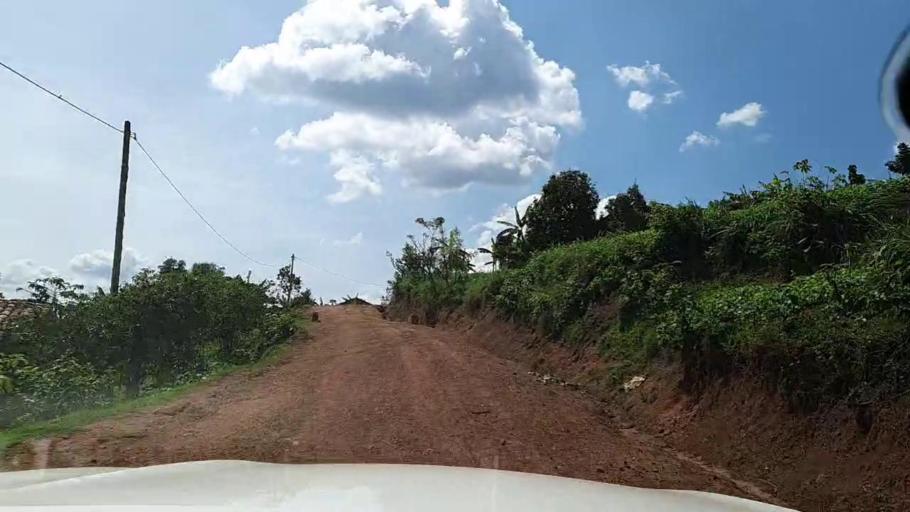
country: RW
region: Southern Province
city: Butare
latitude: -2.7465
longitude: 29.7051
